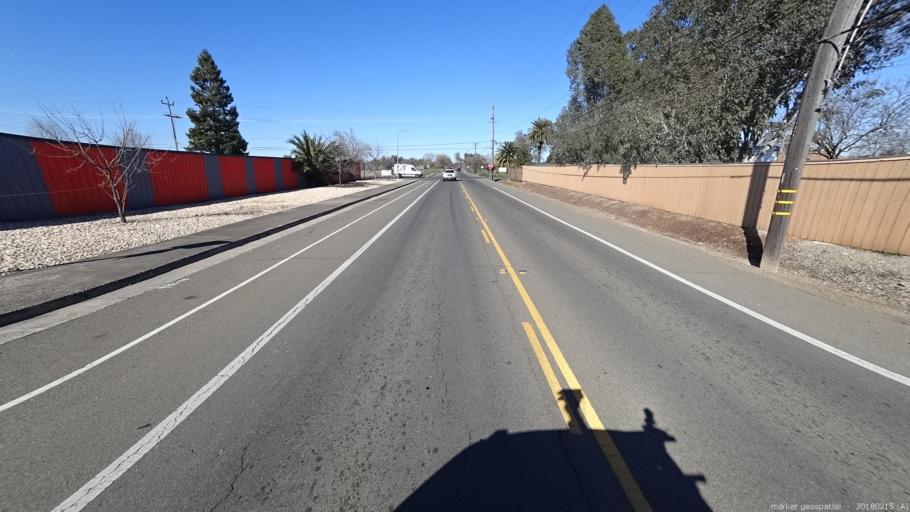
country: US
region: California
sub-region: Sacramento County
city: North Highlands
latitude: 38.6971
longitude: -121.4014
